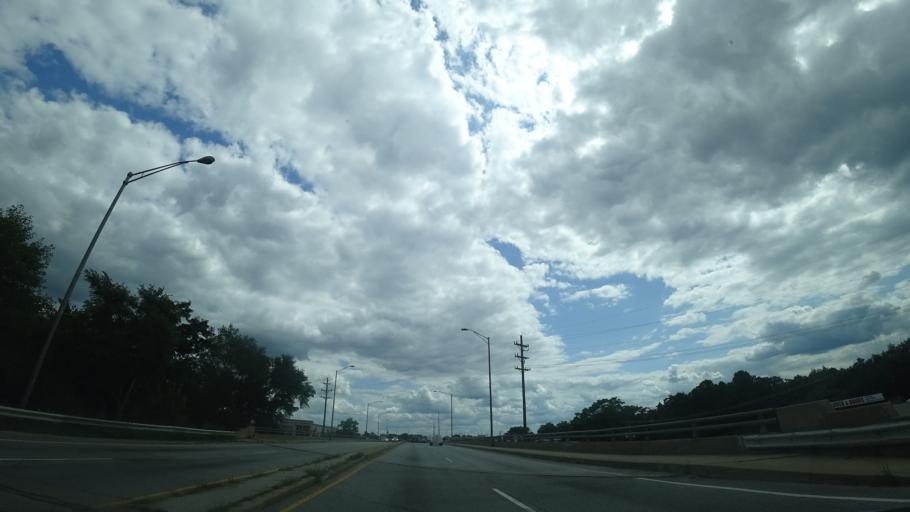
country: US
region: Illinois
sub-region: Cook County
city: Alsip
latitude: 41.6796
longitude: -87.7389
